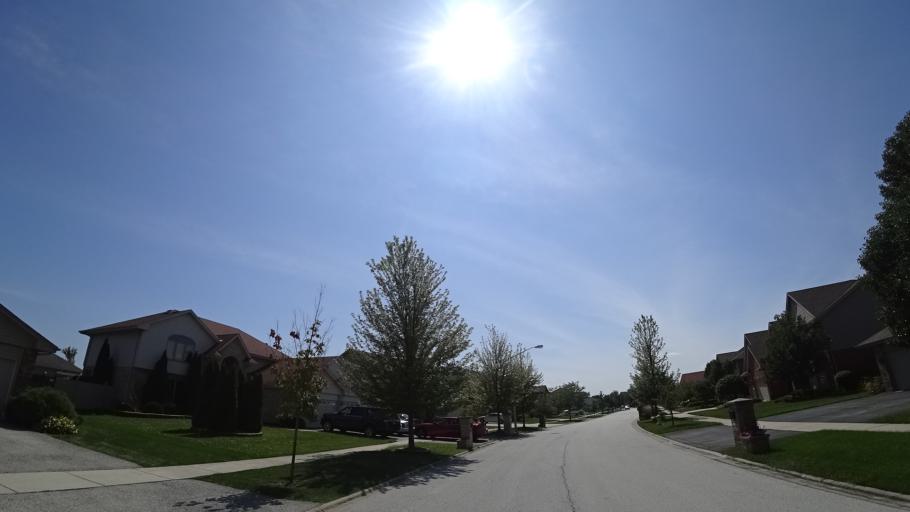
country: US
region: Illinois
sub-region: Cook County
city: Orland Hills
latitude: 41.5628
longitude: -87.8295
